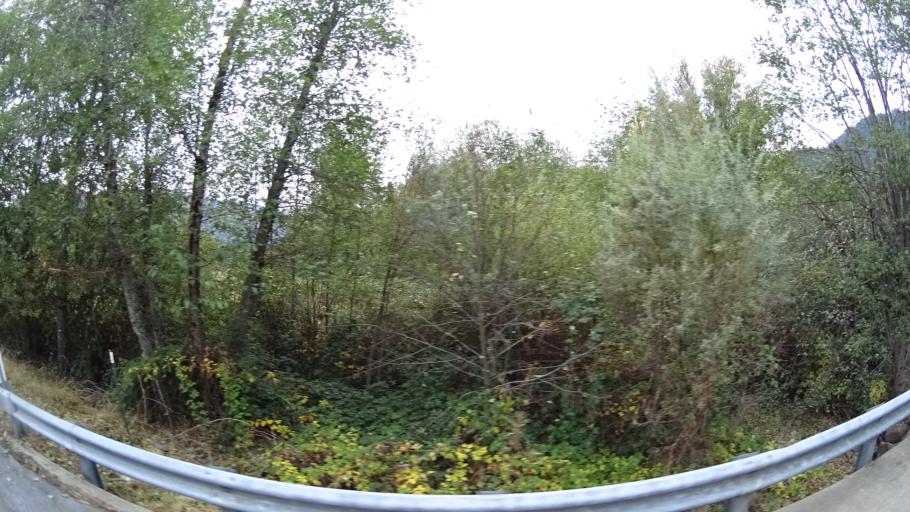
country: US
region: California
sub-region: Siskiyou County
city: Happy Camp
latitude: 41.8411
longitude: -123.2113
